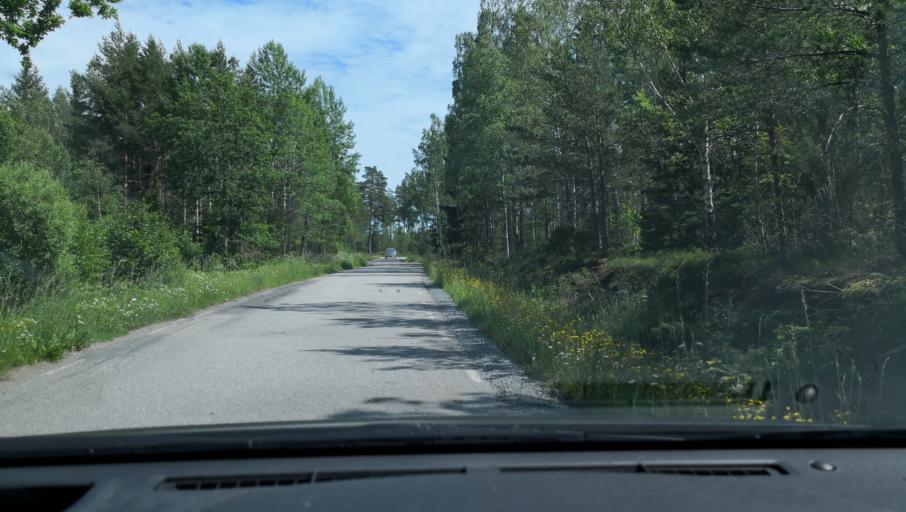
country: SE
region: Uppsala
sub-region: Uppsala Kommun
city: Alsike
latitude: 59.7060
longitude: 17.6736
